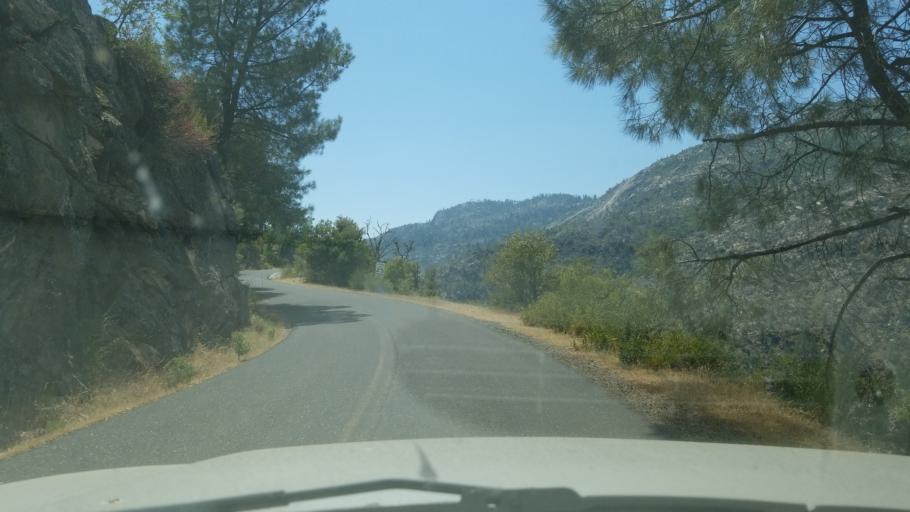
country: US
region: California
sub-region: Mariposa County
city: Yosemite Valley
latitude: 37.9409
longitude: -119.7881
